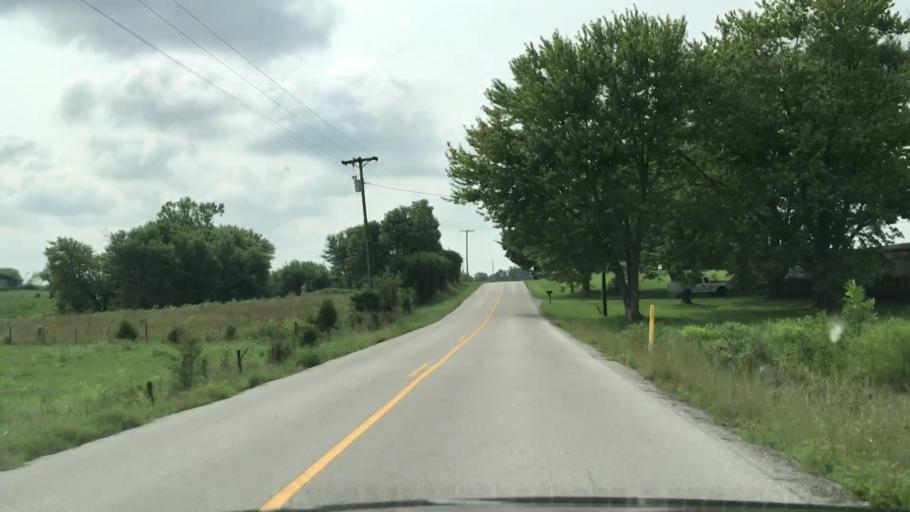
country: US
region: Kentucky
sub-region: Edmonson County
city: Brownsville
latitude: 37.1097
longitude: -86.1475
